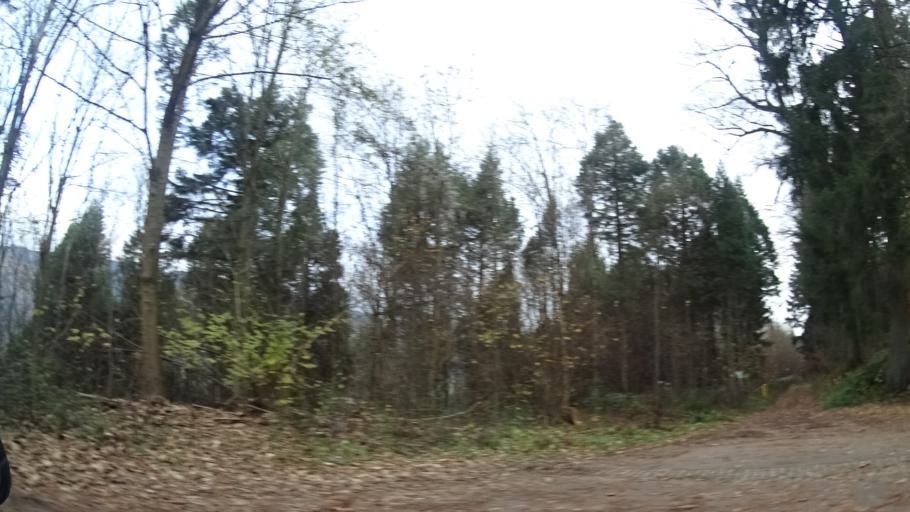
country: DE
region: Baden-Wuerttemberg
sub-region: Karlsruhe Region
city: Zwingenberg
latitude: 49.4136
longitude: 9.0269
